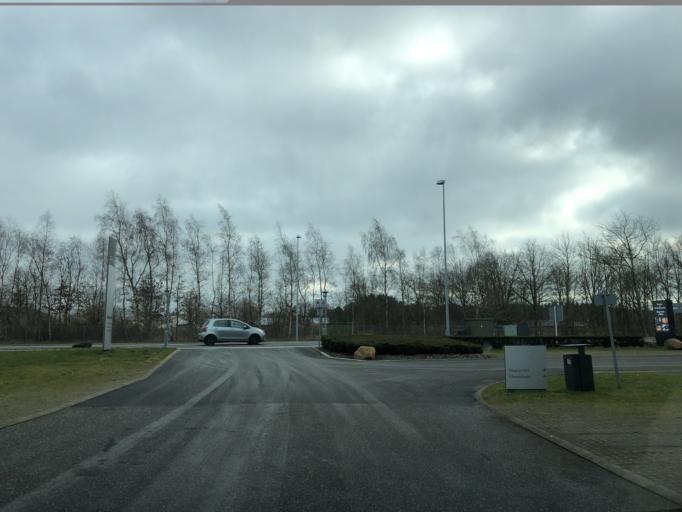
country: DK
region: South Denmark
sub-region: Billund Kommune
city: Billund
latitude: 55.7316
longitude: 9.1328
